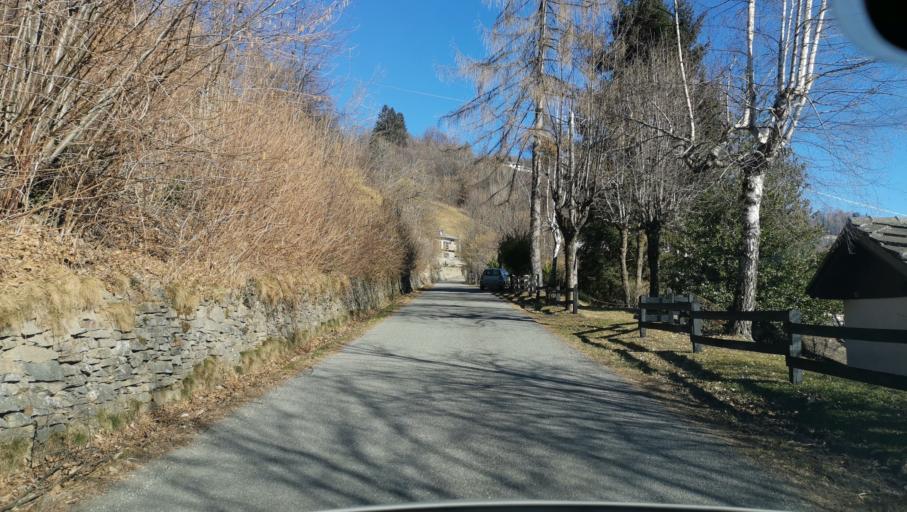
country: IT
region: Piedmont
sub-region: Provincia di Torino
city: Rora
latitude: 44.7922
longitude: 7.1946
